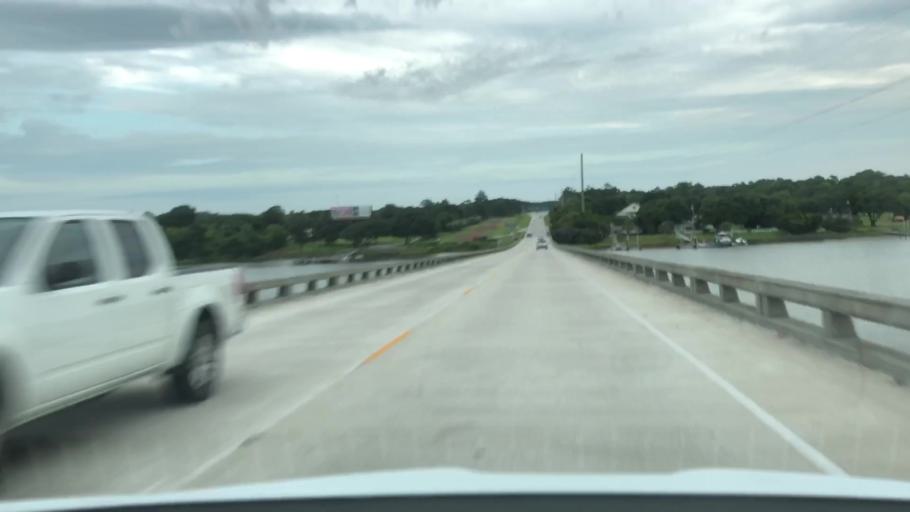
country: US
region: North Carolina
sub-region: Carteret County
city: Cedar Point
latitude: 34.6770
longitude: -77.0663
